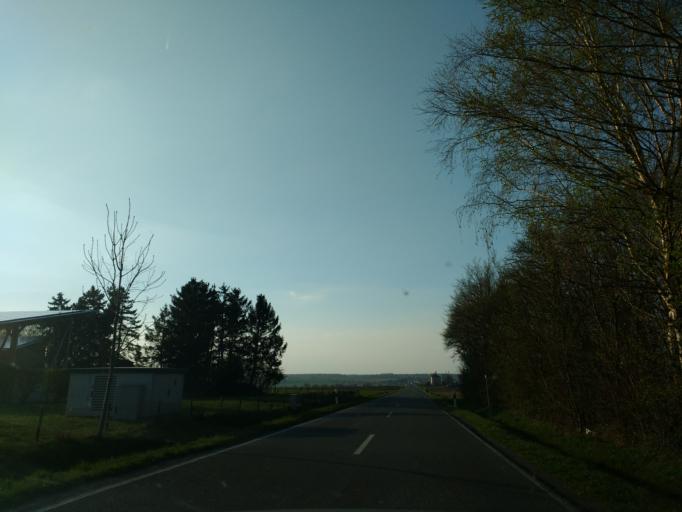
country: DE
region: North Rhine-Westphalia
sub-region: Regierungsbezirk Detmold
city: Paderborn
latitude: 51.6362
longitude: 8.7159
